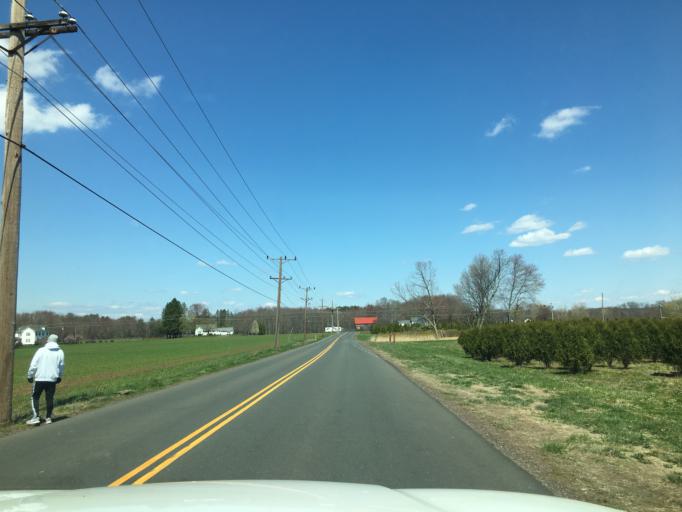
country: US
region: Connecticut
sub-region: Hartford County
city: Hazardville
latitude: 42.0000
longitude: -72.5301
